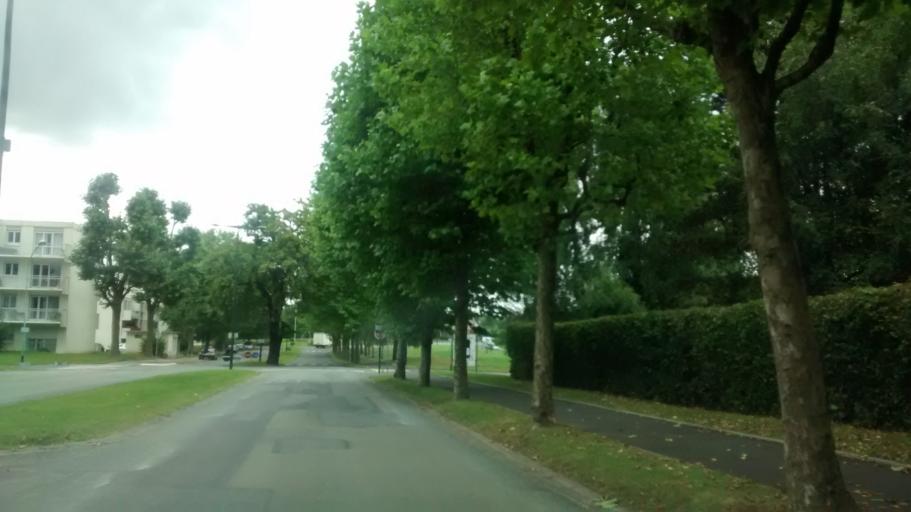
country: FR
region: Haute-Normandie
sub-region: Departement de la Seine-Maritime
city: Bois-Guillaume
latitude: 49.4685
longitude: 1.1414
